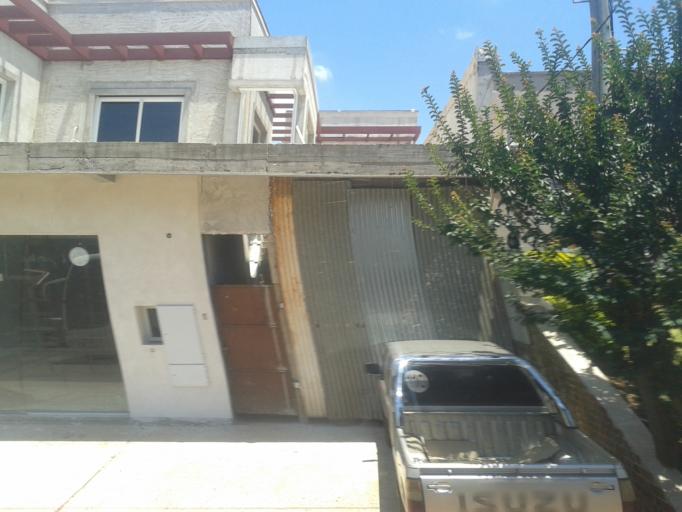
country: AR
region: Misiones
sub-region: Departamento de Leandro N. Alem
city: Leandro N. Alem
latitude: -27.6122
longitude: -55.3279
